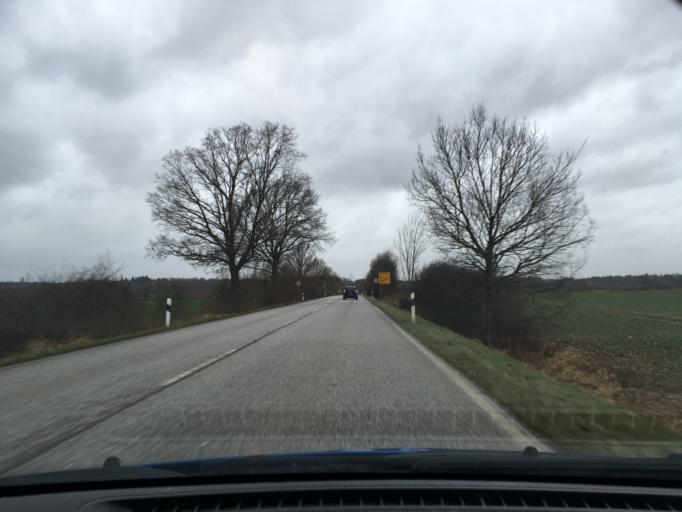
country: DE
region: Schleswig-Holstein
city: Schulendorf
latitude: 53.4700
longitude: 10.5381
